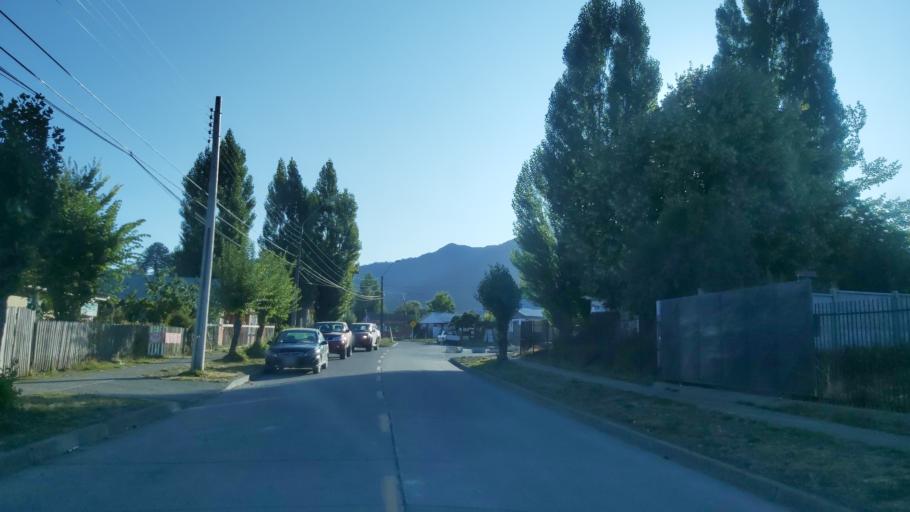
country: AR
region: Neuquen
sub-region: Departamento de Loncopue
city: Loncopue
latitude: -38.4498
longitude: -71.3702
